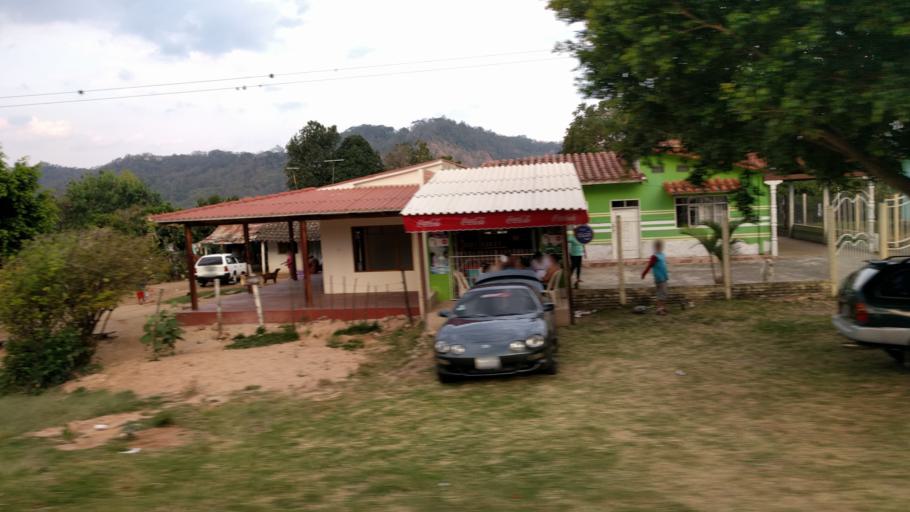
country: BO
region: Santa Cruz
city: Jorochito
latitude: -18.1109
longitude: -63.4589
